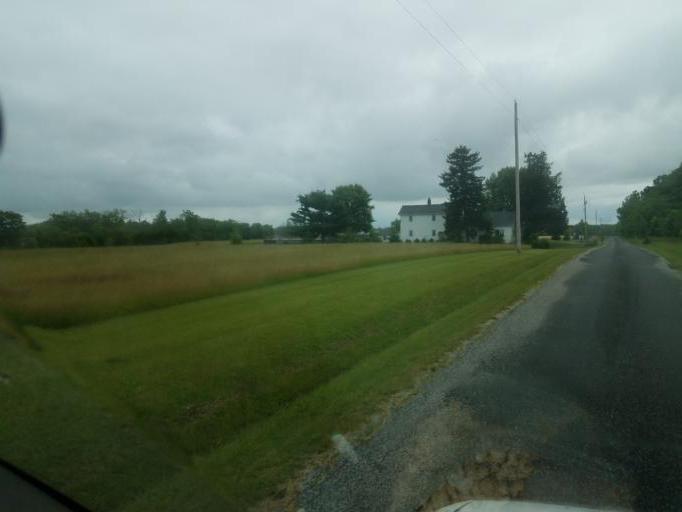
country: US
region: Ohio
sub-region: Marion County
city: Marion
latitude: 40.5436
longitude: -83.0387
